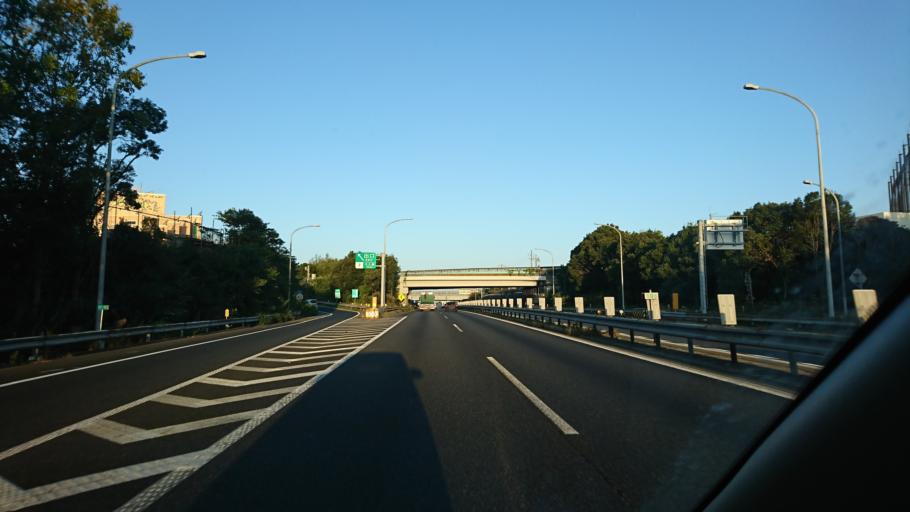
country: JP
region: Hyogo
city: Akashi
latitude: 34.7094
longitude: 134.9453
